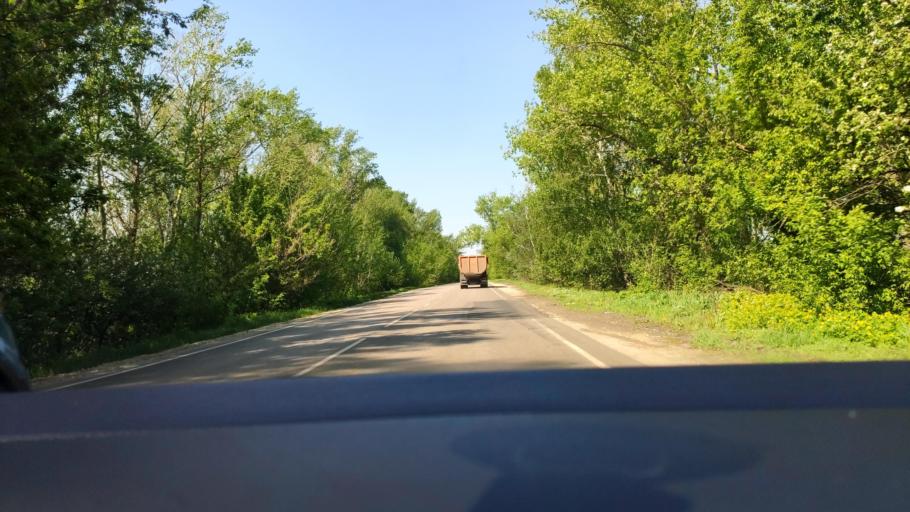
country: RU
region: Voronezj
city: Maslovka
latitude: 51.5303
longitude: 39.3049
